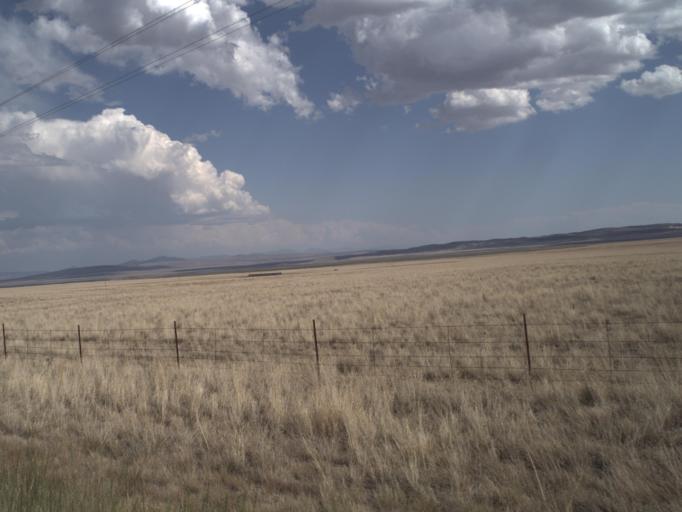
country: US
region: Idaho
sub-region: Power County
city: American Falls
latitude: 41.9683
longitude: -113.0979
